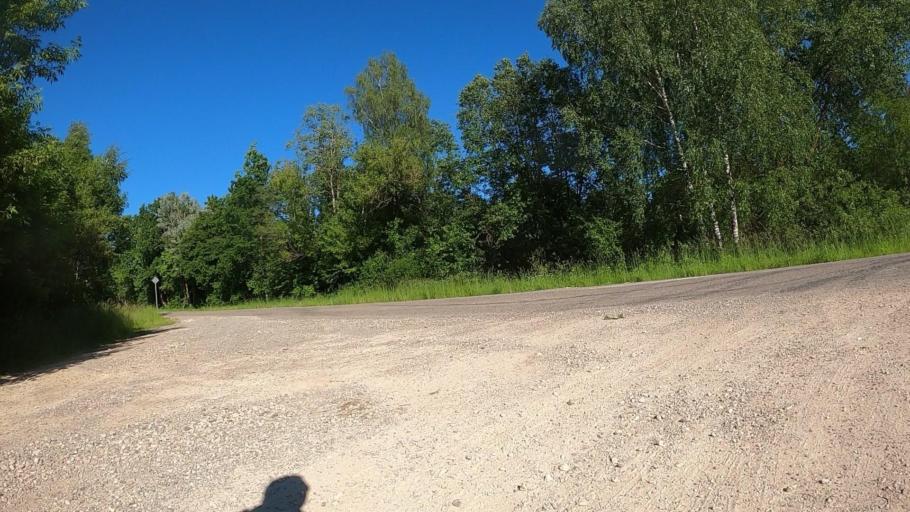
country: LV
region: Ogre
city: Ogre
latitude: 56.7811
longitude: 24.6594
